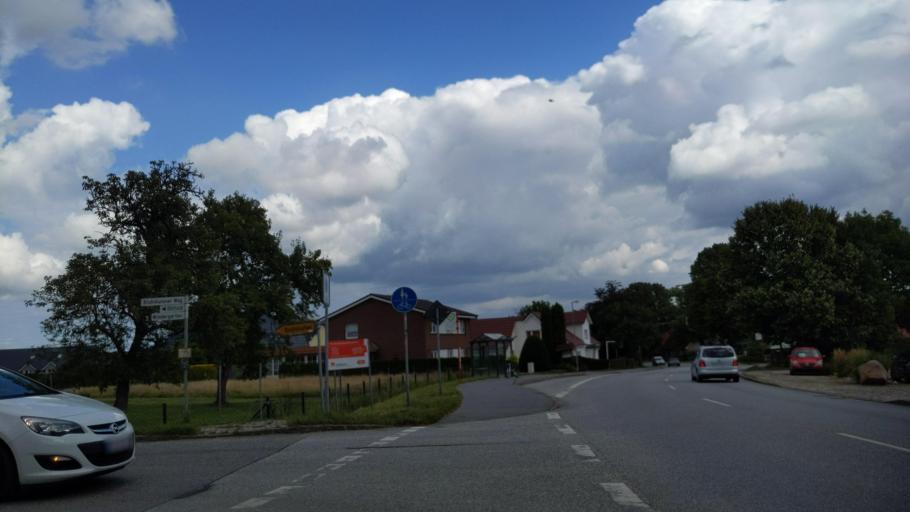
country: DE
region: Schleswig-Holstein
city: Reinfeld
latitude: 53.8272
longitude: 10.5083
